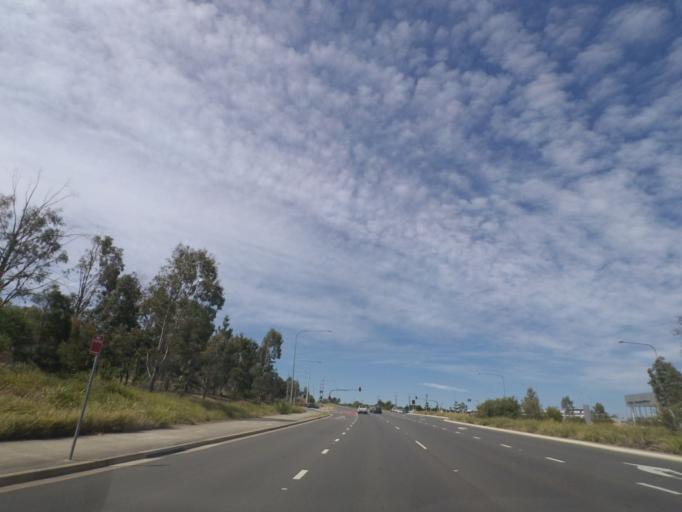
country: AU
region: New South Wales
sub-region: Camden
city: Narellan
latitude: -34.0306
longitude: 150.7517
